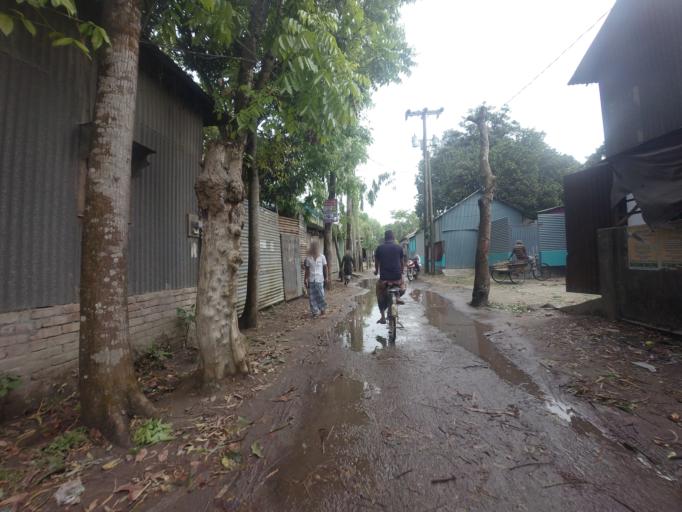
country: BD
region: Rajshahi
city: Sirajganj
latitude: 24.3257
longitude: 89.6870
